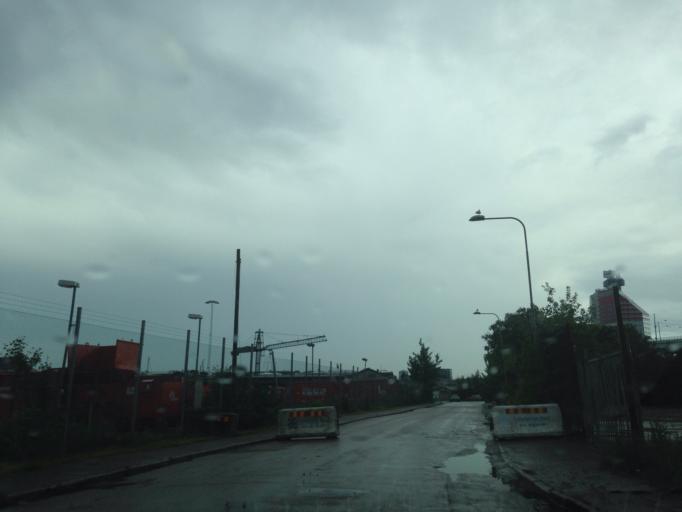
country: SE
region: Vaestra Goetaland
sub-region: Goteborg
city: Goeteborg
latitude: 57.7174
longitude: 11.9652
